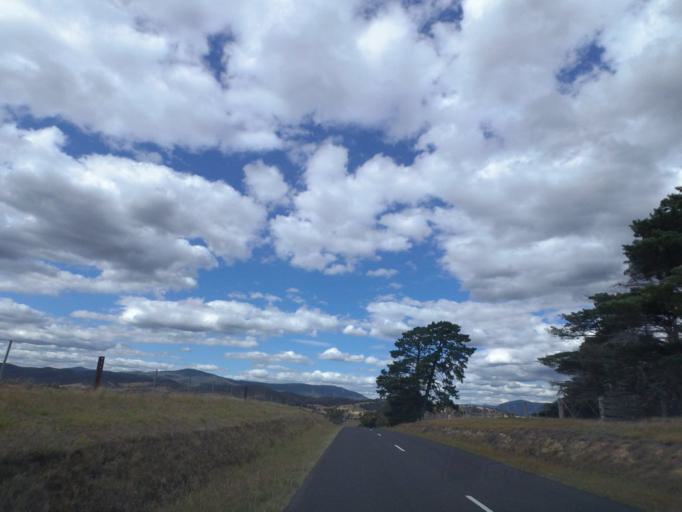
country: AU
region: Victoria
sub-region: Yarra Ranges
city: Yarra Glen
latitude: -37.6396
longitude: 145.4258
